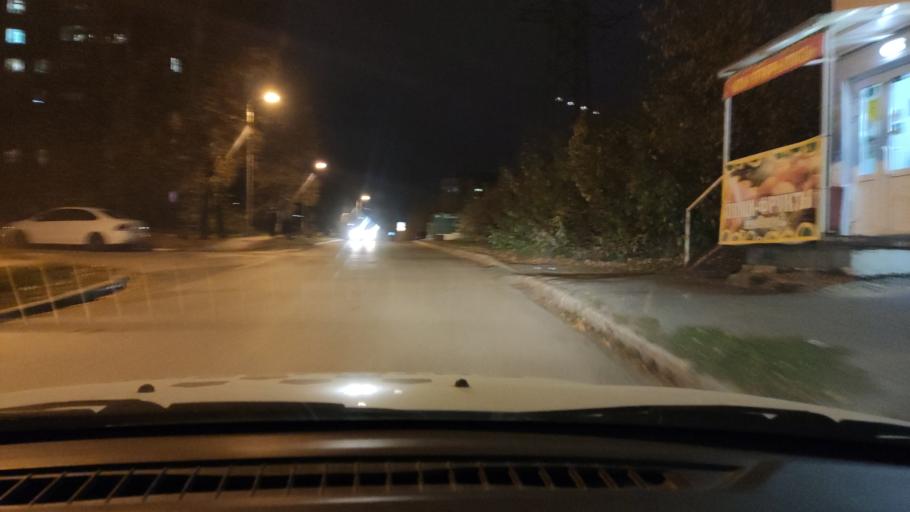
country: RU
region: Perm
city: Perm
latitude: 57.9792
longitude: 56.2216
